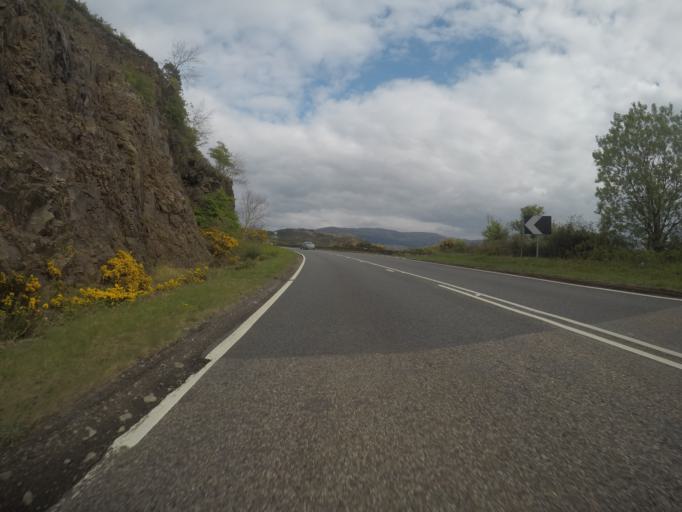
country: GB
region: Scotland
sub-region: Highland
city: Portree
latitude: 57.2834
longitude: -5.6381
